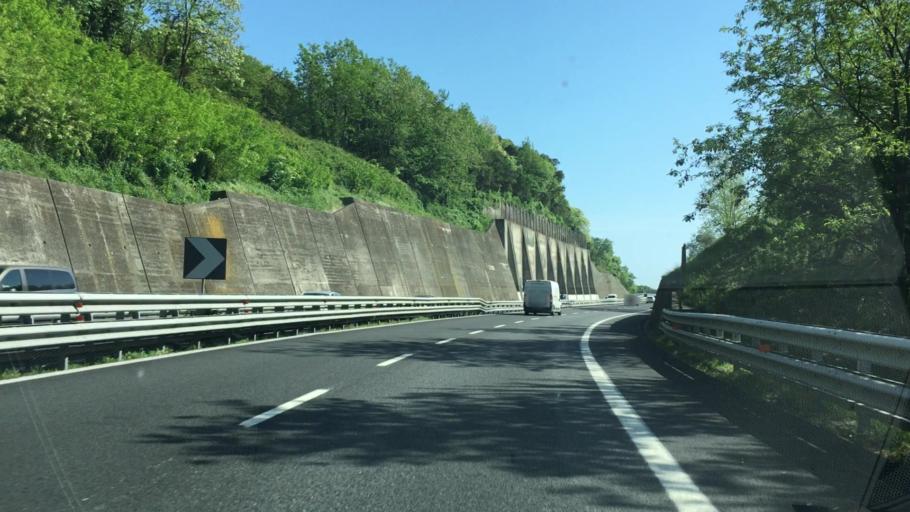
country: IT
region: Liguria
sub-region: Provincia di Genova
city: Cogorno
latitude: 44.2999
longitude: 9.3841
